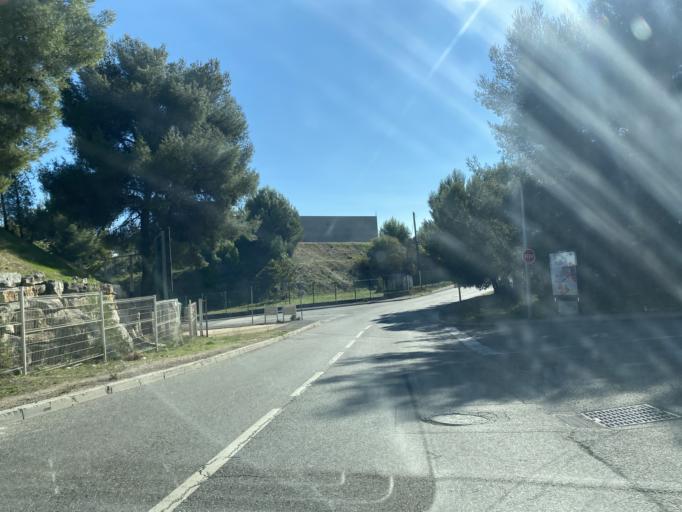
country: FR
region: Provence-Alpes-Cote d'Azur
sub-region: Departement des Bouches-du-Rhone
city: La Ciotat
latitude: 43.2056
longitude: 5.6006
